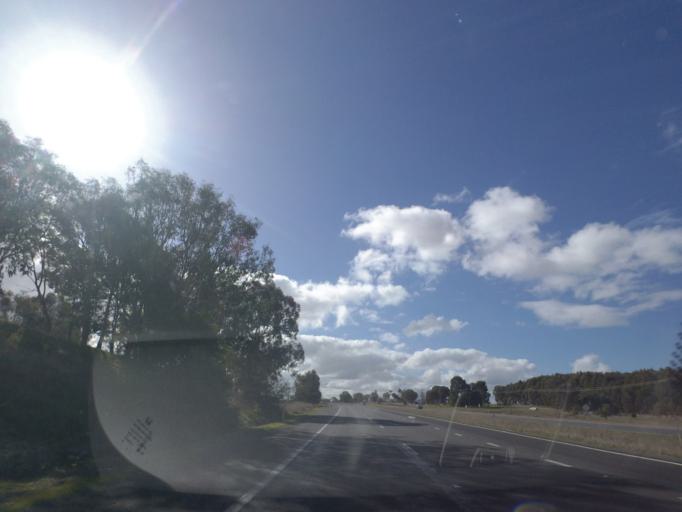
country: AU
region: New South Wales
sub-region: Albury Municipality
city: Lavington
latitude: -35.9737
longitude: 147.0033
